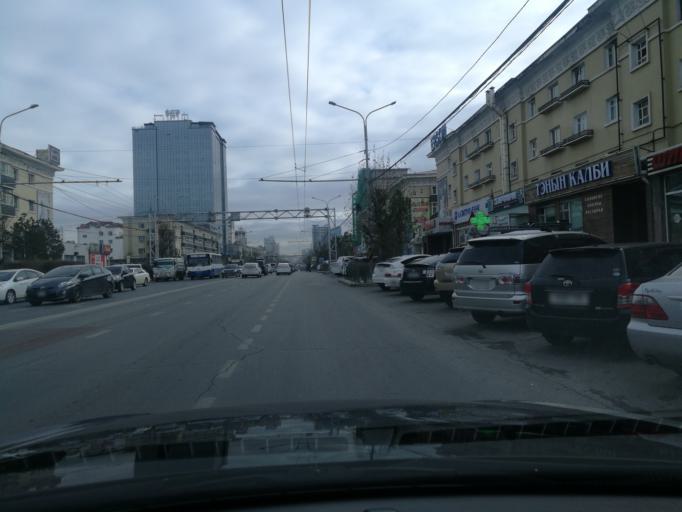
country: MN
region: Ulaanbaatar
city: Ulaanbaatar
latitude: 47.9155
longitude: 106.8989
